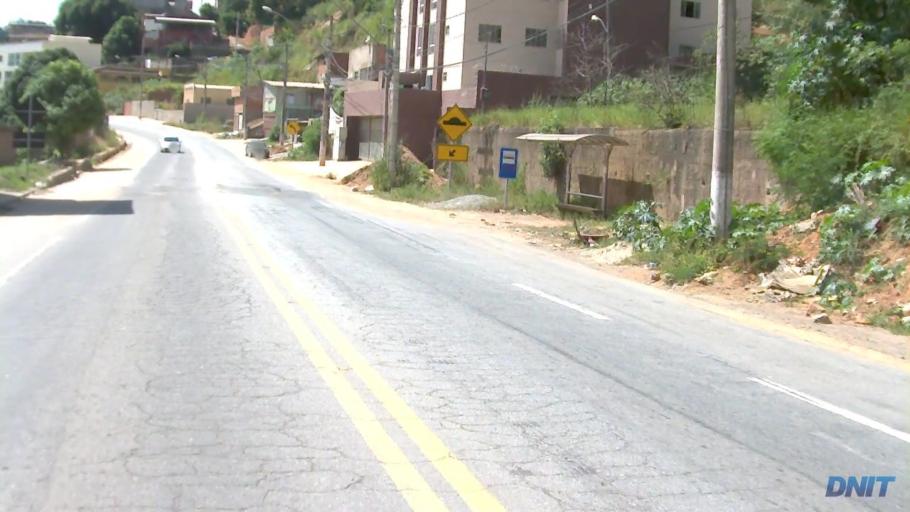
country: BR
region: Minas Gerais
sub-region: Coronel Fabriciano
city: Coronel Fabriciano
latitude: -19.5365
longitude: -42.6690
